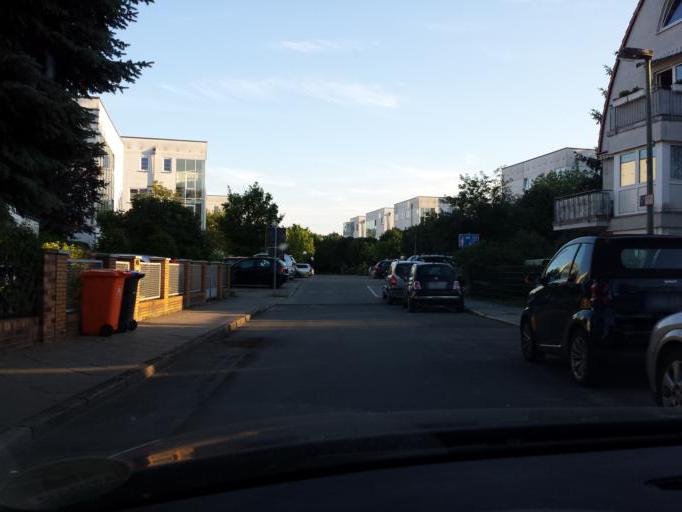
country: DE
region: Berlin
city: Lichtenrade
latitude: 52.4234
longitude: 13.4044
